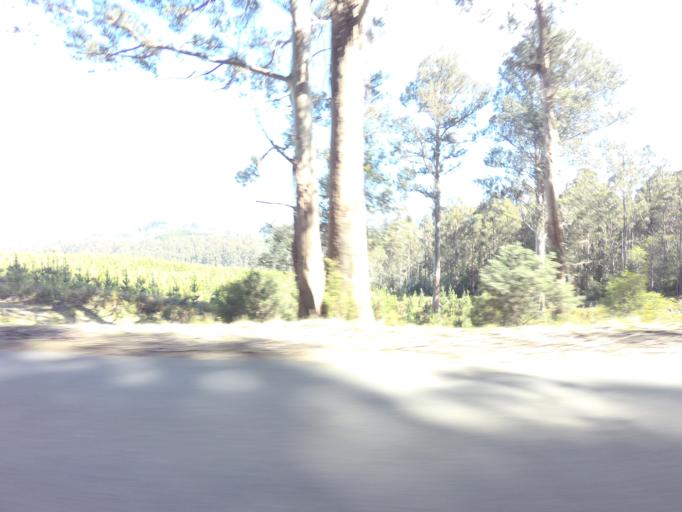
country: AU
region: Tasmania
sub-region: Derwent Valley
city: New Norfolk
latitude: -42.7402
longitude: 146.6609
